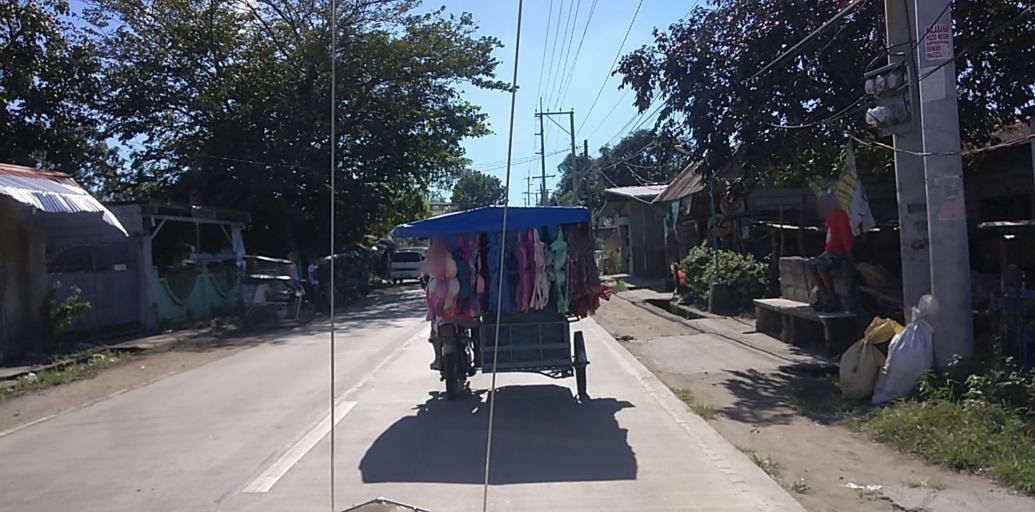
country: PH
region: Central Luzon
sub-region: Province of Pampanga
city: San Luis
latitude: 15.0558
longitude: 120.7774
